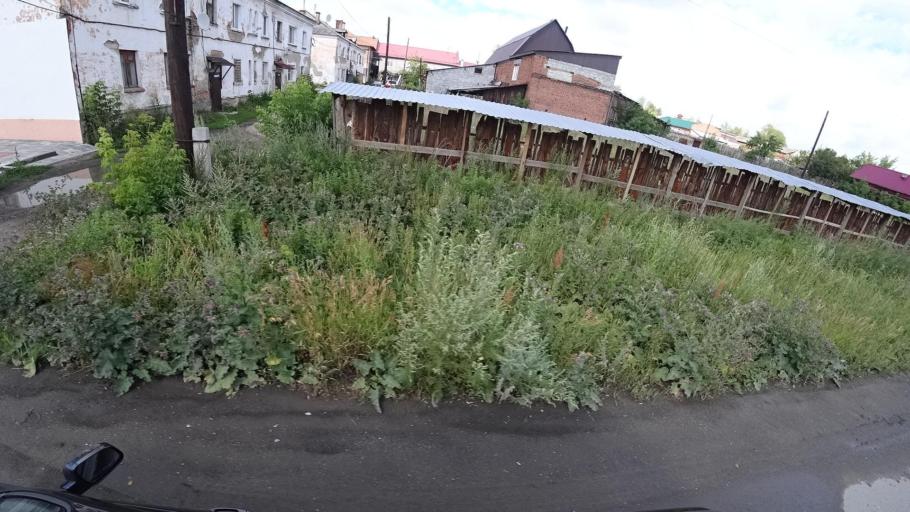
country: RU
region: Sverdlovsk
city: Kamyshlov
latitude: 56.8455
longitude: 62.7114
